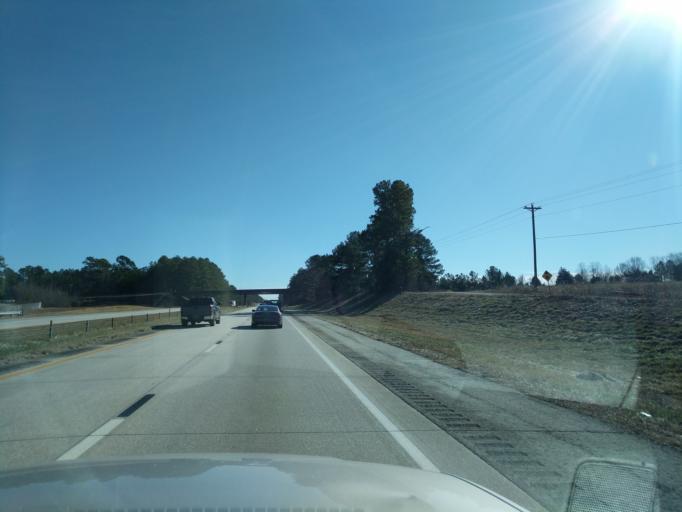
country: US
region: South Carolina
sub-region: Laurens County
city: Watts Mills
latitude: 34.5321
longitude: -81.9346
